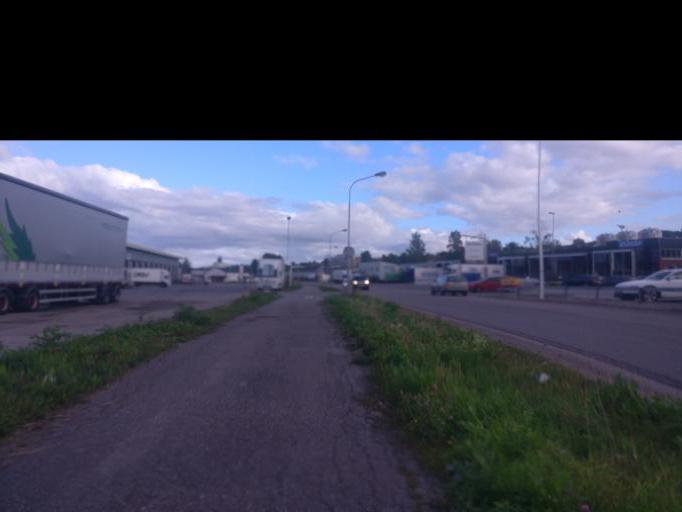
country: SE
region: Vaesternorrland
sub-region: Sundsvalls Kommun
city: Sundsvall
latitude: 62.3871
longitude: 17.3228
